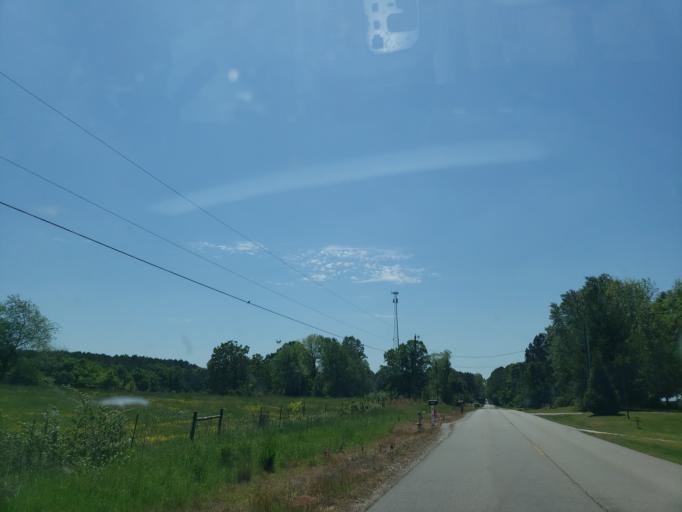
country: US
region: Alabama
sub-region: Madison County
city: Harvest
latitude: 34.9252
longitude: -86.7299
